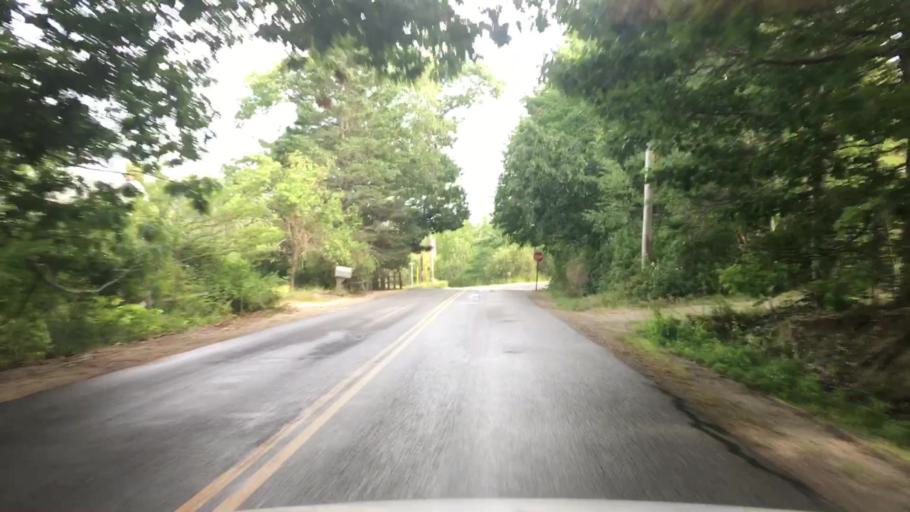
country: US
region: Maine
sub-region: Hancock County
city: Trenton
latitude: 44.4361
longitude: -68.3982
